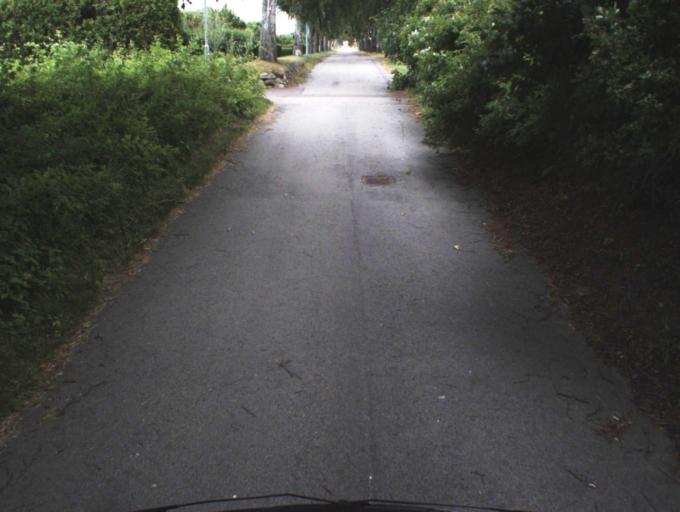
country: SE
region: Skane
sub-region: Helsingborg
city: Rydeback
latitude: 55.9711
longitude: 12.7722
